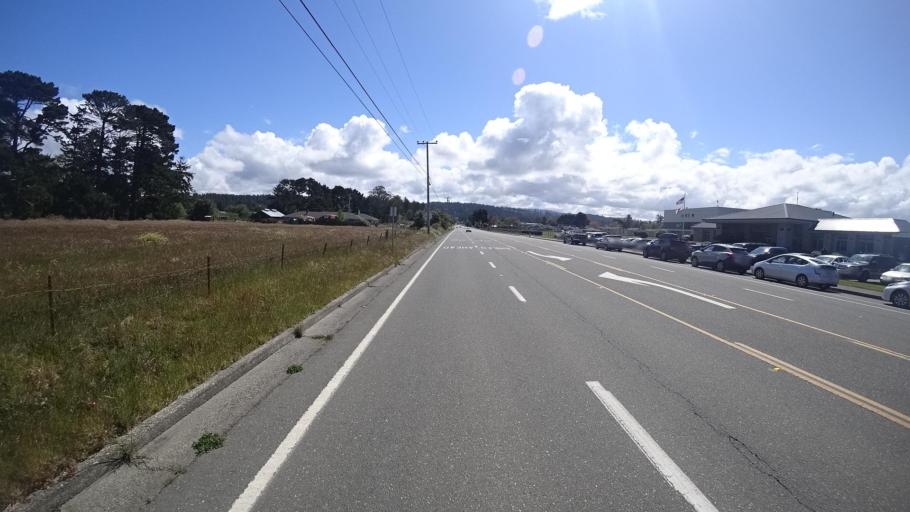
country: US
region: California
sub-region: Humboldt County
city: McKinleyville
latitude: 40.9563
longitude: -124.1090
